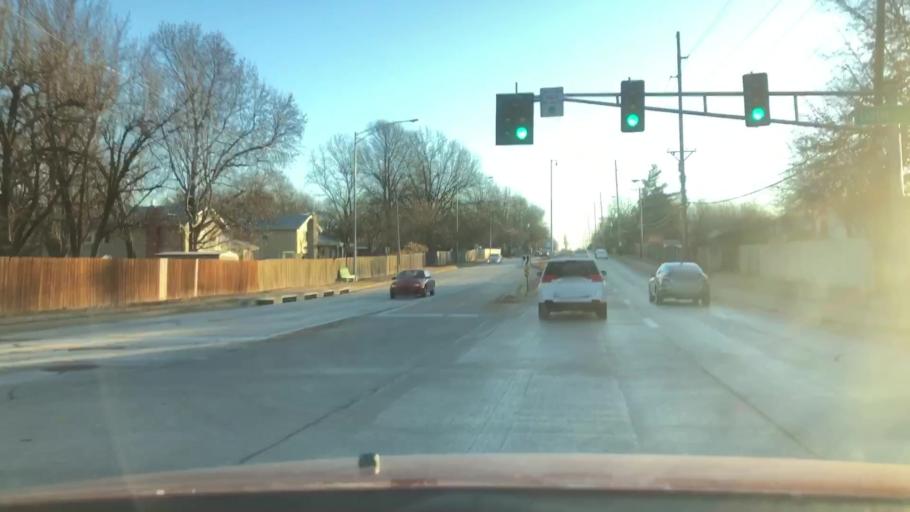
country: US
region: Missouri
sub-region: Greene County
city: Springfield
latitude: 37.1591
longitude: -93.2565
